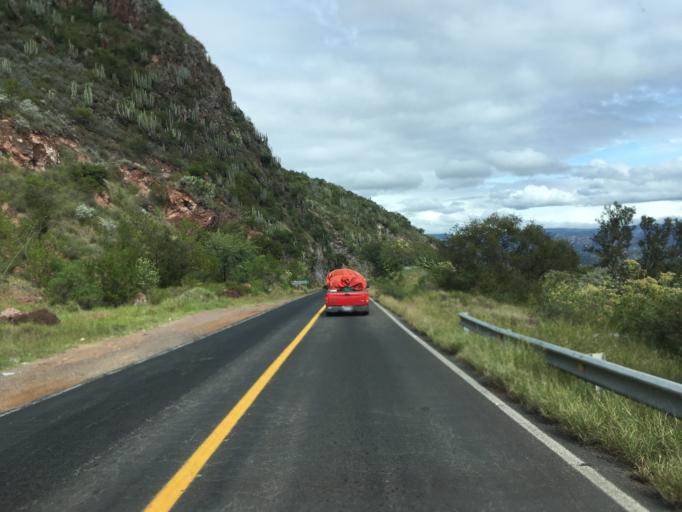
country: MX
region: Hidalgo
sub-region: San Agustin Metzquititlan
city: Mezquititlan
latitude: 20.4324
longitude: -98.6855
